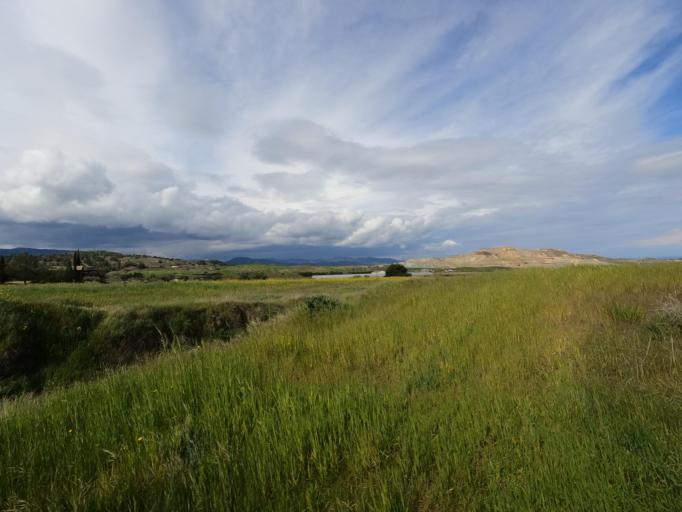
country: CY
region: Lefkosia
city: Lefka
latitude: 35.0812
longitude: 32.9258
